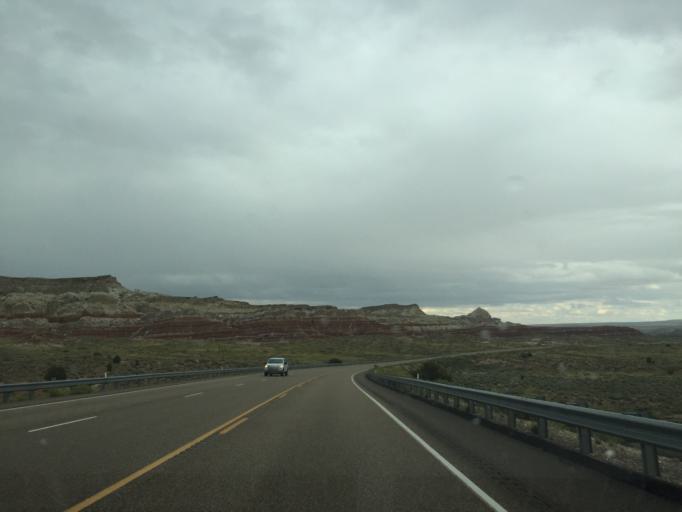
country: US
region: Arizona
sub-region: Coconino County
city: Page
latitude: 37.1278
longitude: -111.9576
